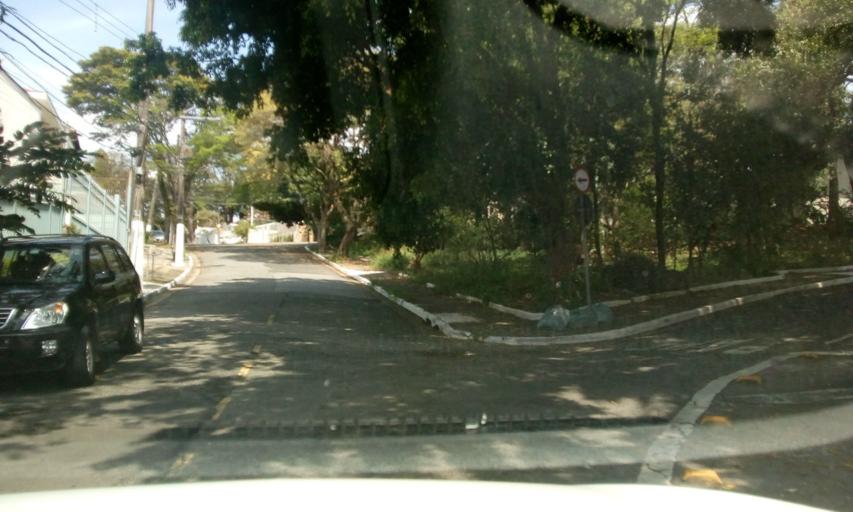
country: BR
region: Sao Paulo
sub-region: Sao Paulo
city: Sao Paulo
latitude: -23.5337
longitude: -46.7101
